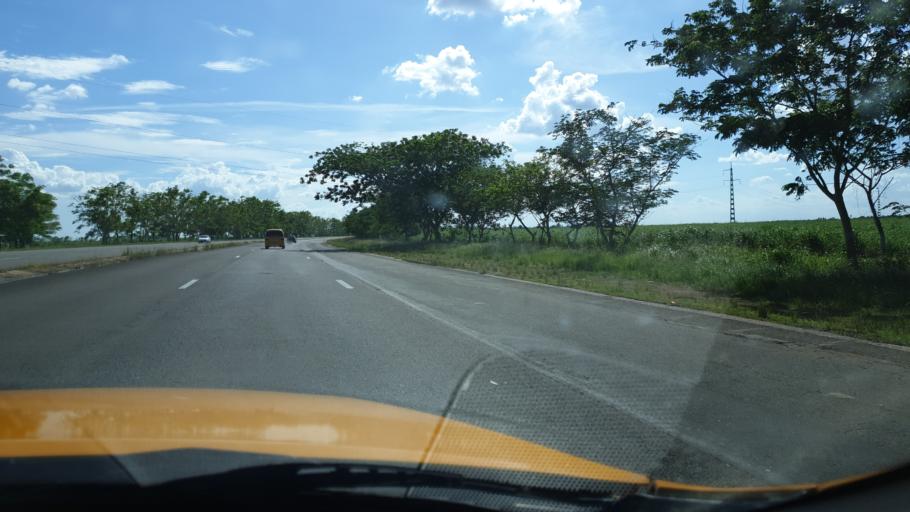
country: CU
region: Cienfuegos
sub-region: Municipio de Aguada de Pasajeros
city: Aguada de Pasajeros
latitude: 22.4026
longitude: -80.8482
